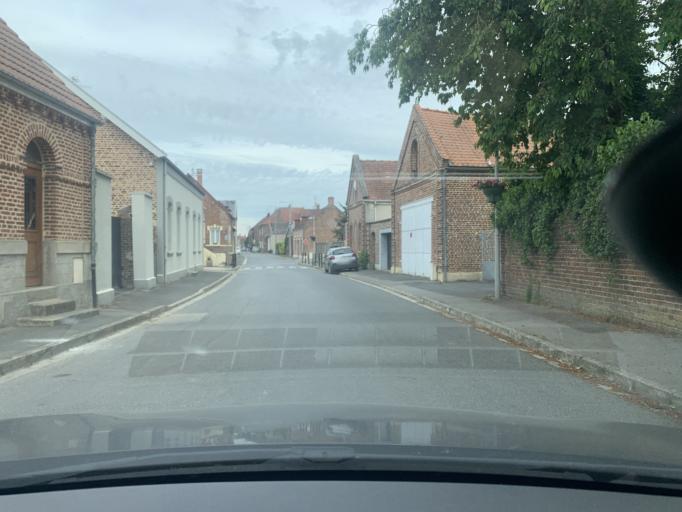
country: FR
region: Nord-Pas-de-Calais
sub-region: Departement du Nord
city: Marcoing
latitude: 50.1388
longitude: 3.1827
